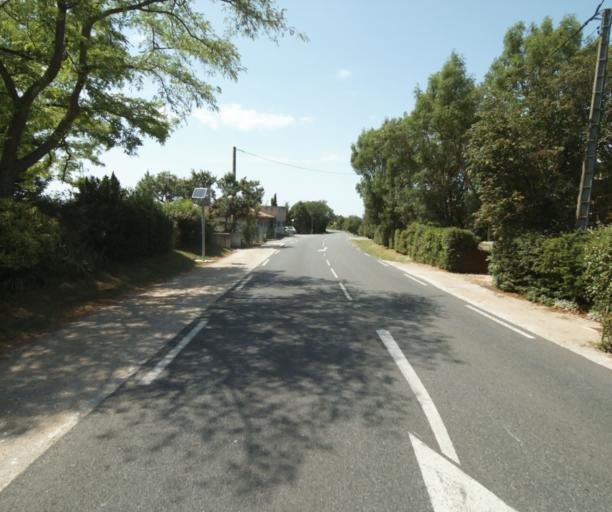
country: FR
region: Midi-Pyrenees
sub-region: Departement de la Haute-Garonne
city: Saint-Felix-Lauragais
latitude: 43.4513
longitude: 1.8808
